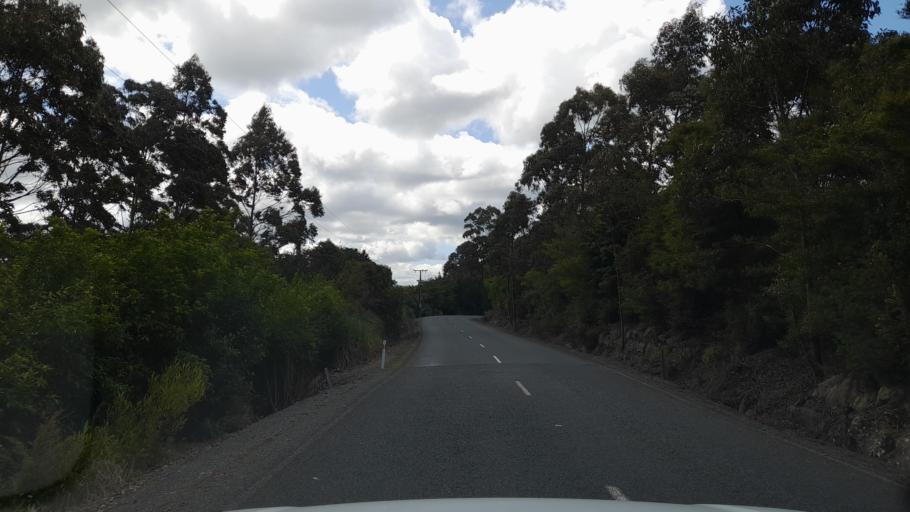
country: NZ
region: Northland
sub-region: Whangarei
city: Maungatapere
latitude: -35.6883
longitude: 174.0418
